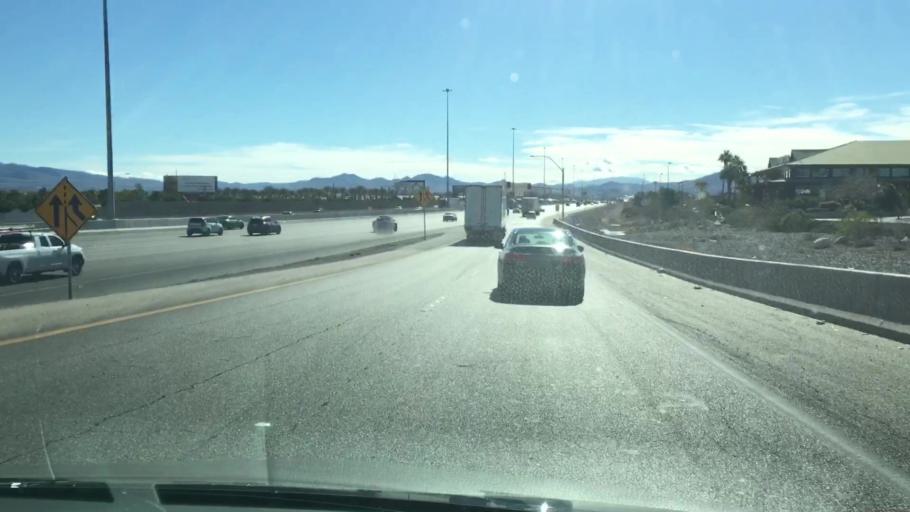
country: US
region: Nevada
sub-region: Clark County
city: Enterprise
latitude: 36.0422
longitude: -115.1813
